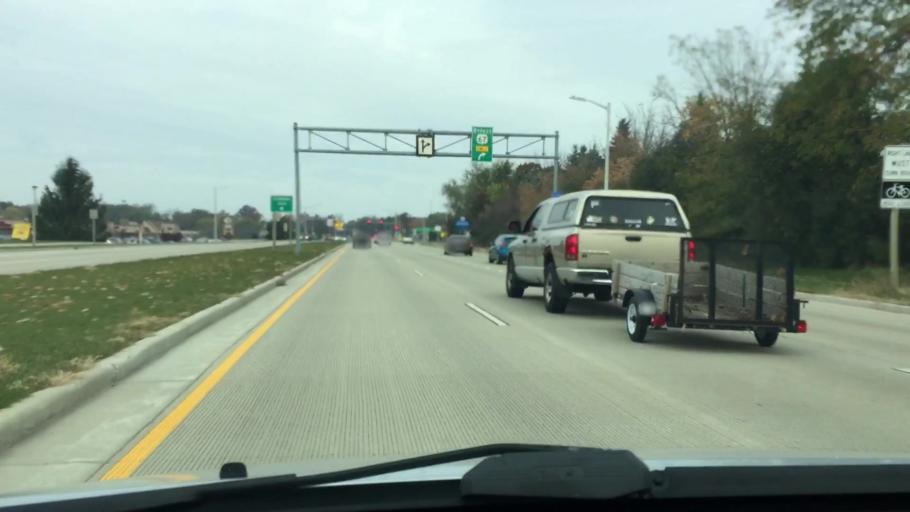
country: US
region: Wisconsin
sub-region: Waukesha County
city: Oconomowoc
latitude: 43.0938
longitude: -88.4787
